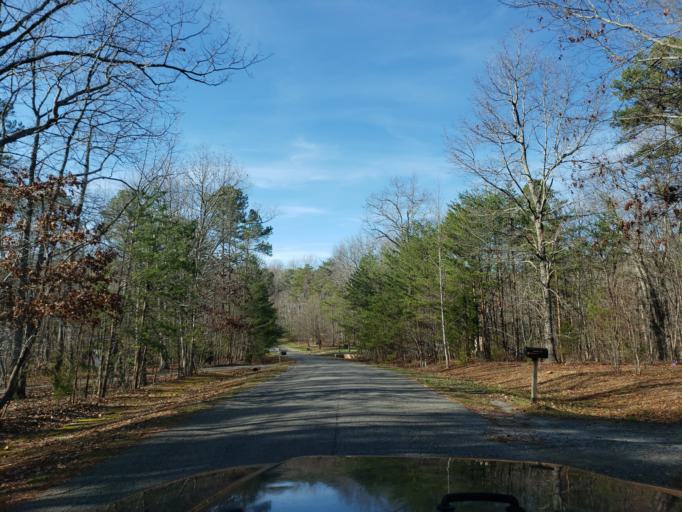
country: US
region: North Carolina
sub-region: Cleveland County
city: White Plains
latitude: 35.1683
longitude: -81.3603
